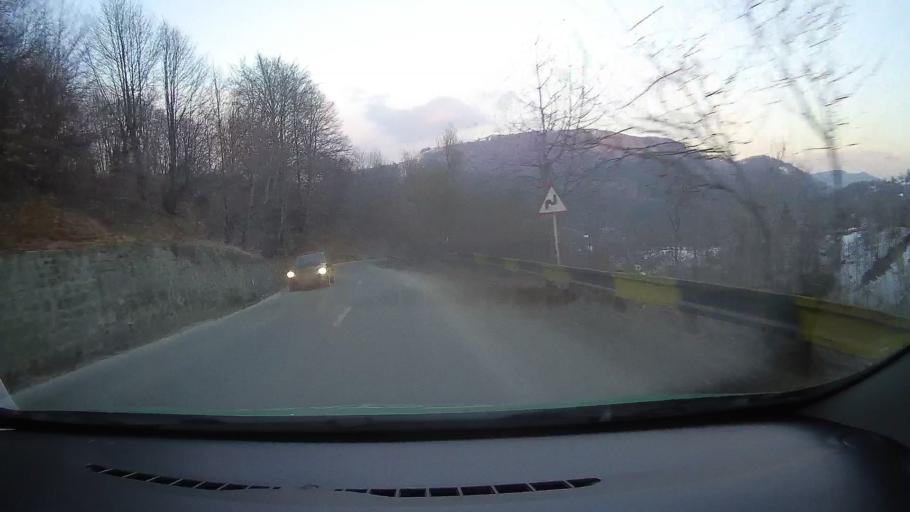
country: RO
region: Prahova
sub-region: Comuna Secaria
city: Secaria
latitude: 45.2697
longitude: 25.6813
